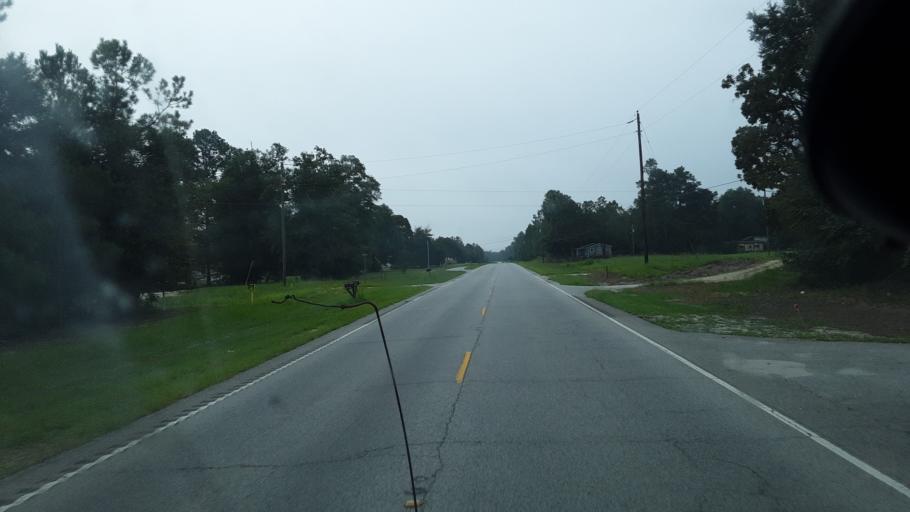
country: US
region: South Carolina
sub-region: Florence County
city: Johnsonville
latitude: 33.9043
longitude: -79.3988
